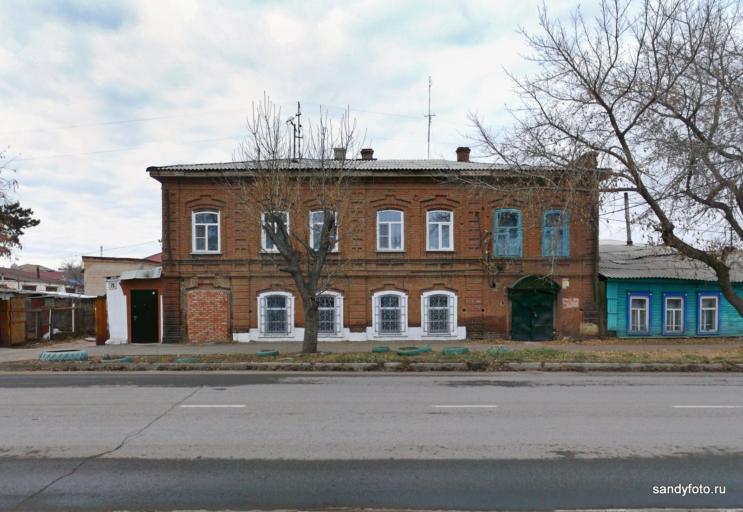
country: RU
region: Chelyabinsk
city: Troitsk
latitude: 54.0822
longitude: 61.5470
